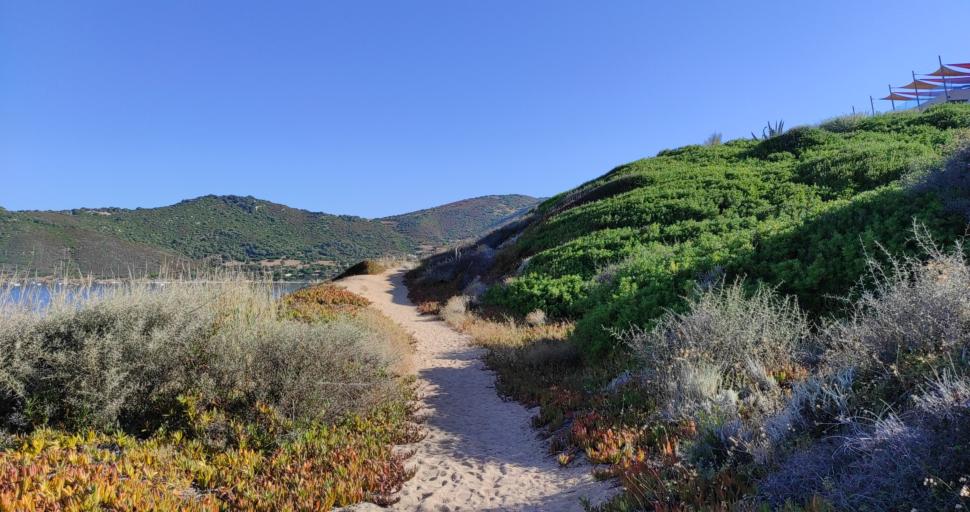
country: FR
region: Corsica
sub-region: Departement de la Corse-du-Sud
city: Alata
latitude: 41.9830
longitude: 8.6696
